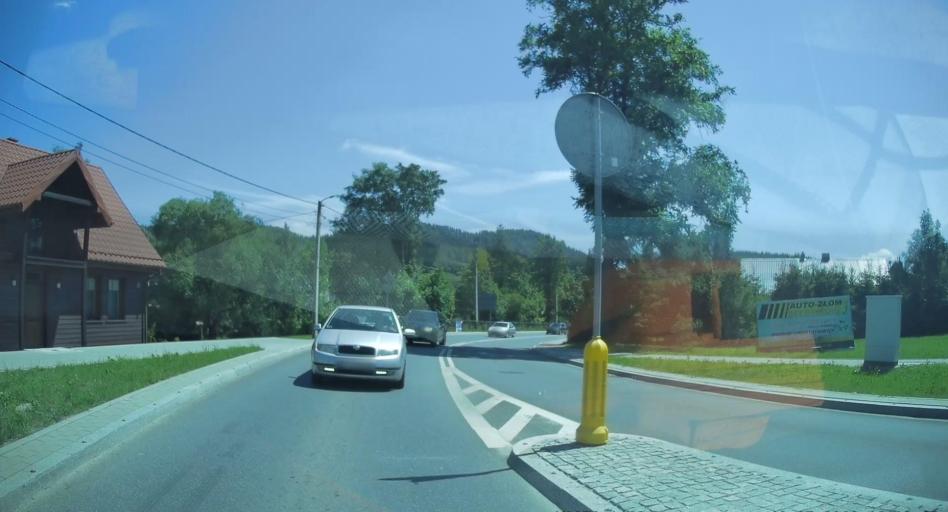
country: PL
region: Lesser Poland Voivodeship
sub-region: Powiat nowosadecki
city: Krynica-Zdroj
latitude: 49.4004
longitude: 20.9556
